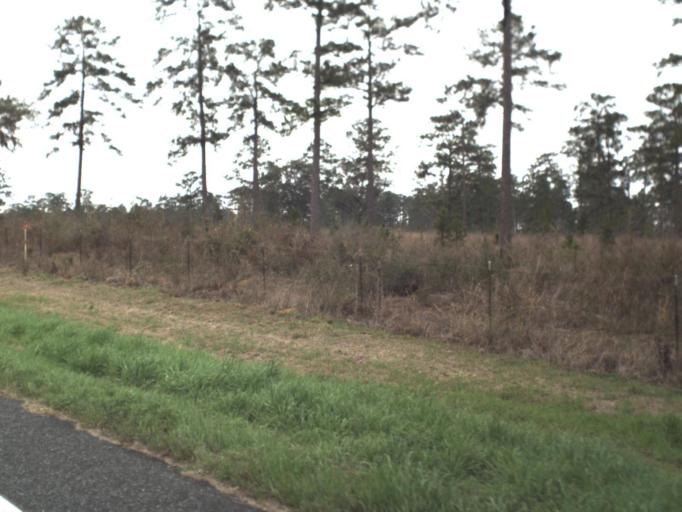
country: US
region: Florida
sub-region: Jefferson County
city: Monticello
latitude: 30.4065
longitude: -84.0008
